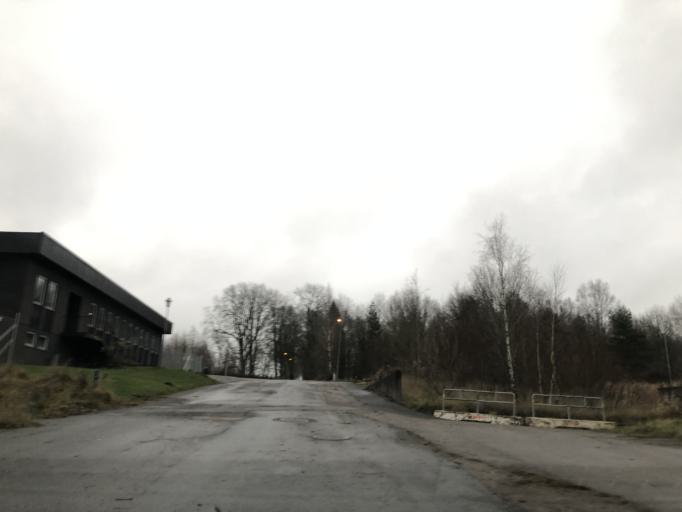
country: SE
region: Vaestra Goetaland
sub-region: Ulricehamns Kommun
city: Ulricehamn
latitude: 57.8423
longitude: 13.2903
